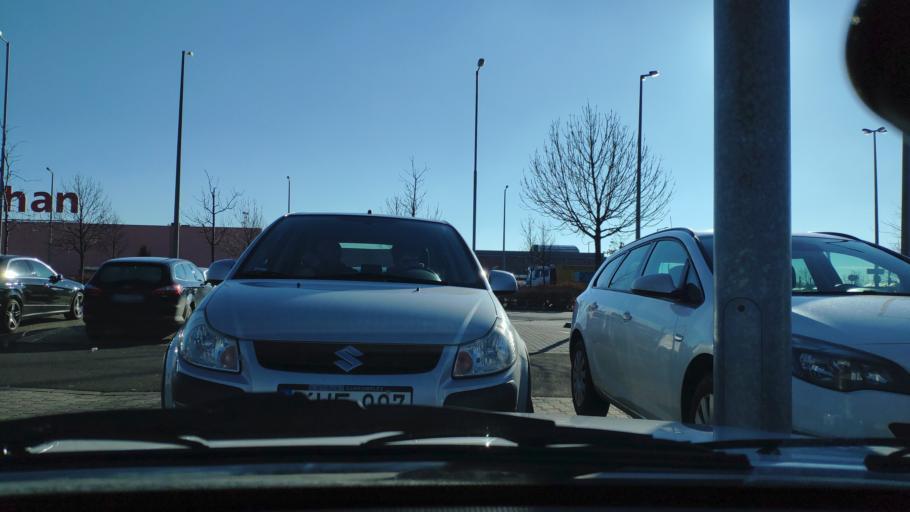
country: HU
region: Budapest
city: Budapest XVIII. keruelet
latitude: 47.4203
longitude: 19.1555
